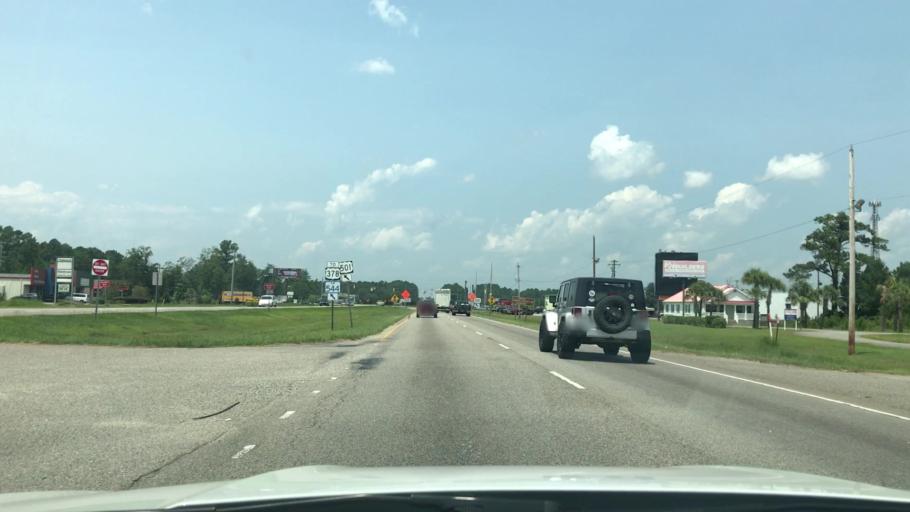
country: US
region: South Carolina
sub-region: Horry County
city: Red Hill
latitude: 33.8031
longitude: -79.0077
